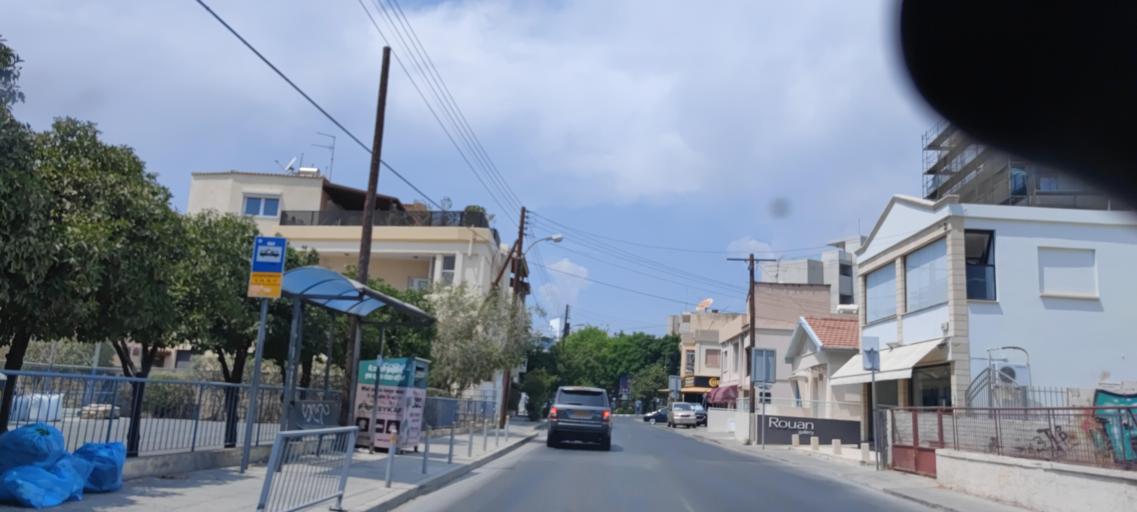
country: CY
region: Limassol
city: Limassol
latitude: 34.6834
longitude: 33.0347
